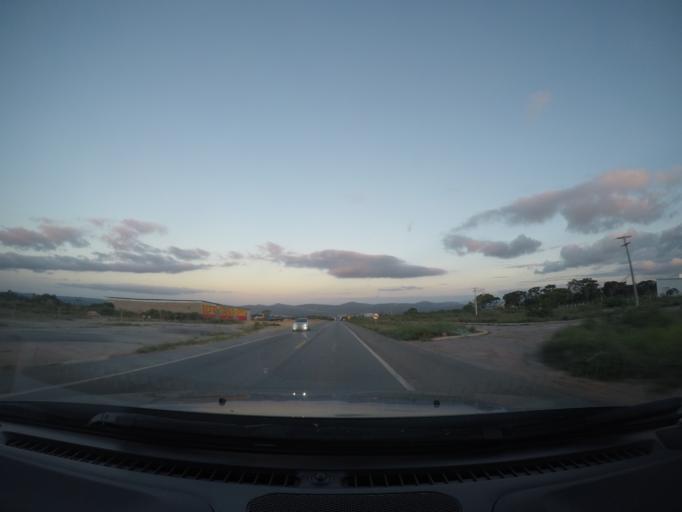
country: BR
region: Bahia
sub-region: Seabra
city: Seabra
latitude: -12.4332
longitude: -41.8136
